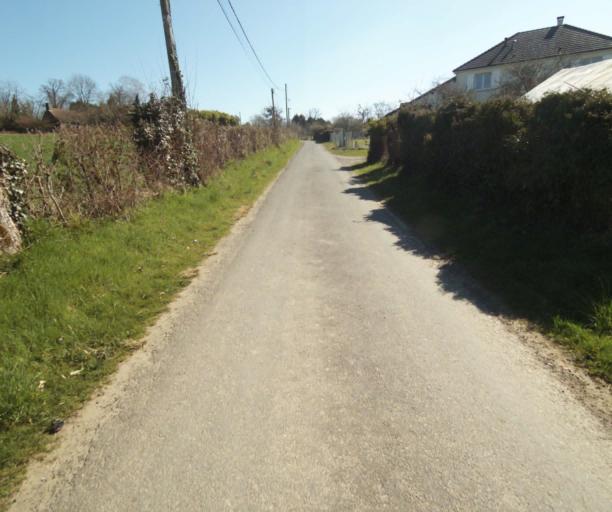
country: FR
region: Limousin
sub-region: Departement de la Correze
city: Saint-Mexant
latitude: 45.3082
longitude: 1.6026
